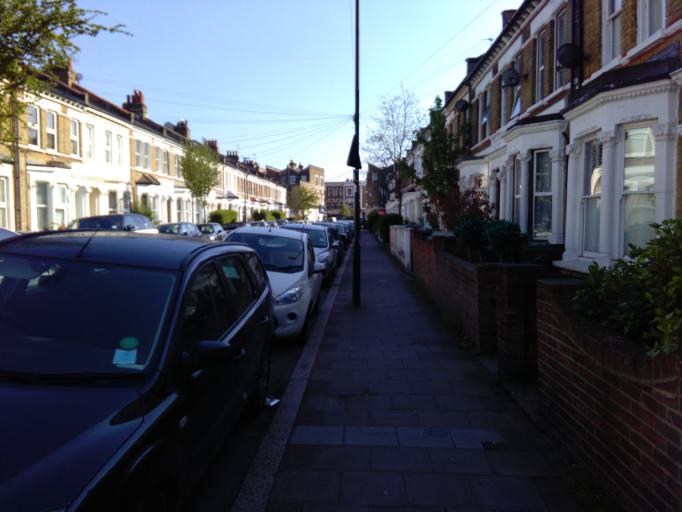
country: GB
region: England
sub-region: Greater London
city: Brixton Hill
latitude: 51.4608
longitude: -0.1253
